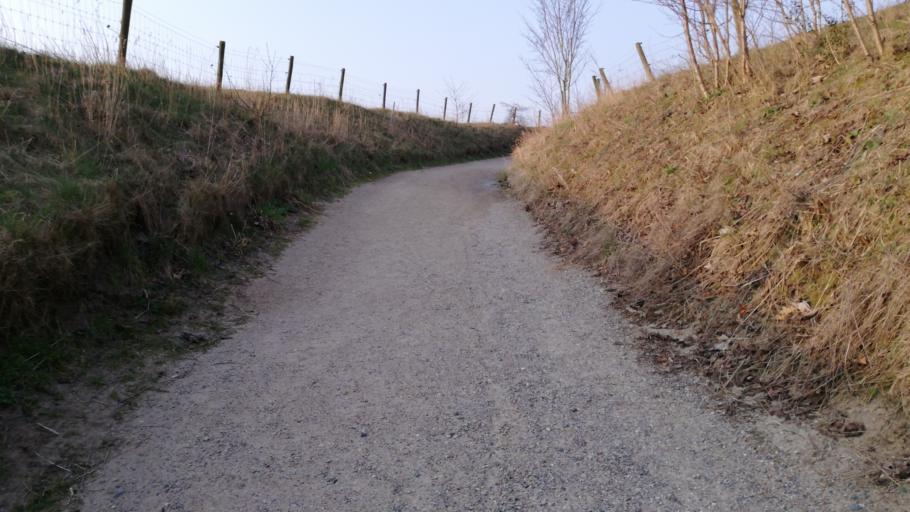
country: SE
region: Skane
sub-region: Ystads Kommun
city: Kopingebro
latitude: 55.3849
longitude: 14.0621
